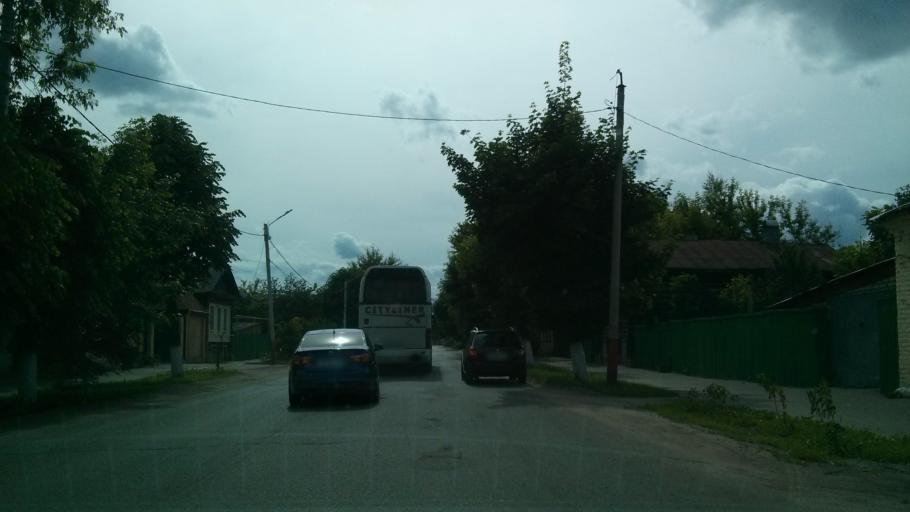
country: RU
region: Vladimir
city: Murom
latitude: 55.5795
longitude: 42.0471
